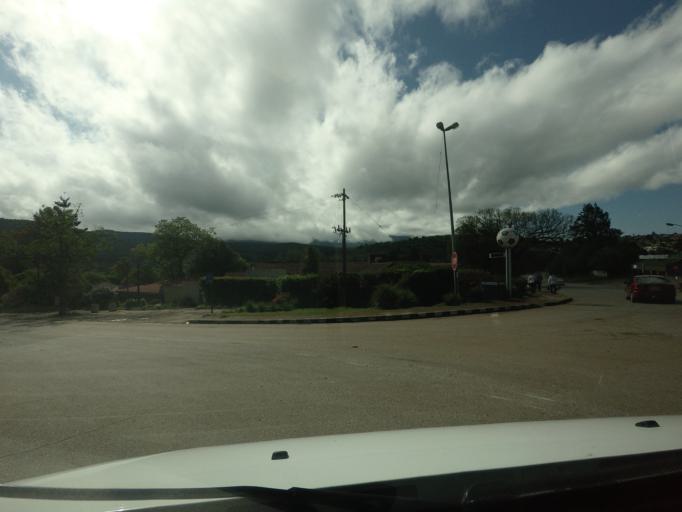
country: ZA
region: Mpumalanga
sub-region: Ehlanzeni District
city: Graksop
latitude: -25.0911
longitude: 30.7784
